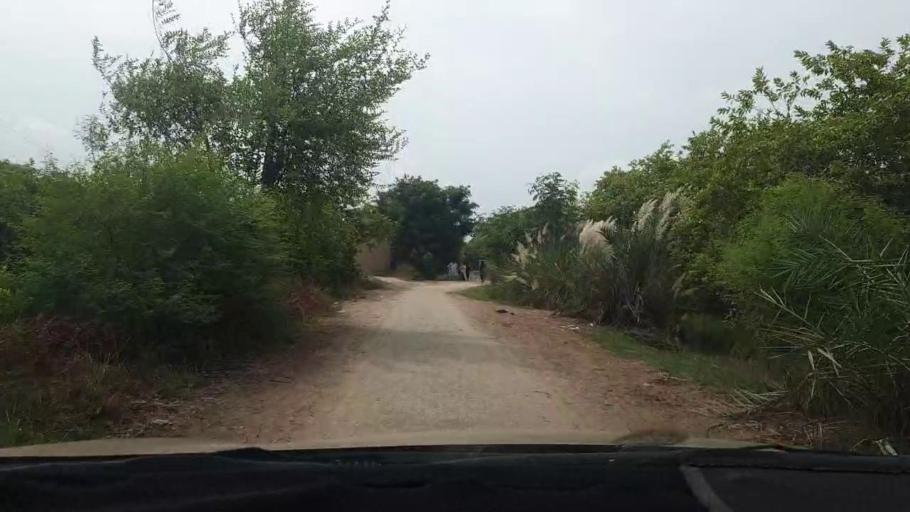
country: PK
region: Sindh
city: Naudero
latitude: 27.6310
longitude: 68.3097
